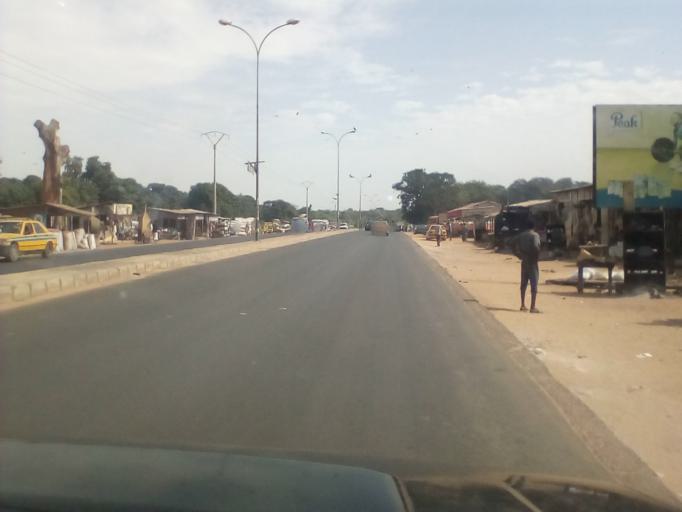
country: GM
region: Western
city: Abuko
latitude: 13.4001
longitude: -16.6517
